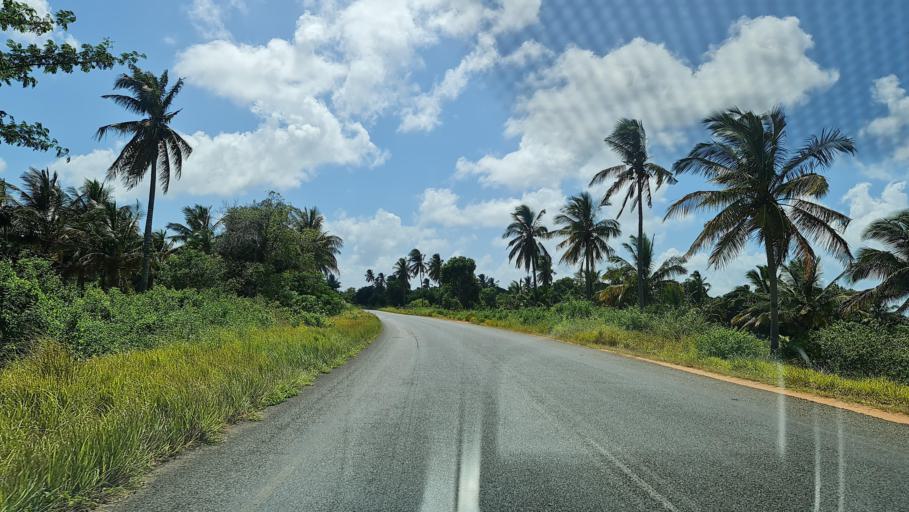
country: MZ
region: Inhambane
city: Maxixe
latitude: -24.5395
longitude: 34.9341
